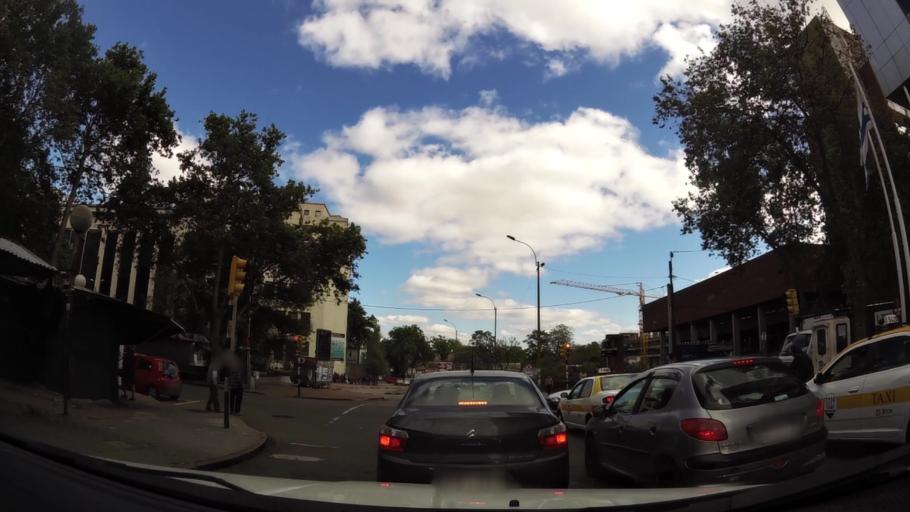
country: UY
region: Montevideo
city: Montevideo
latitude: -34.9007
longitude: -56.1756
